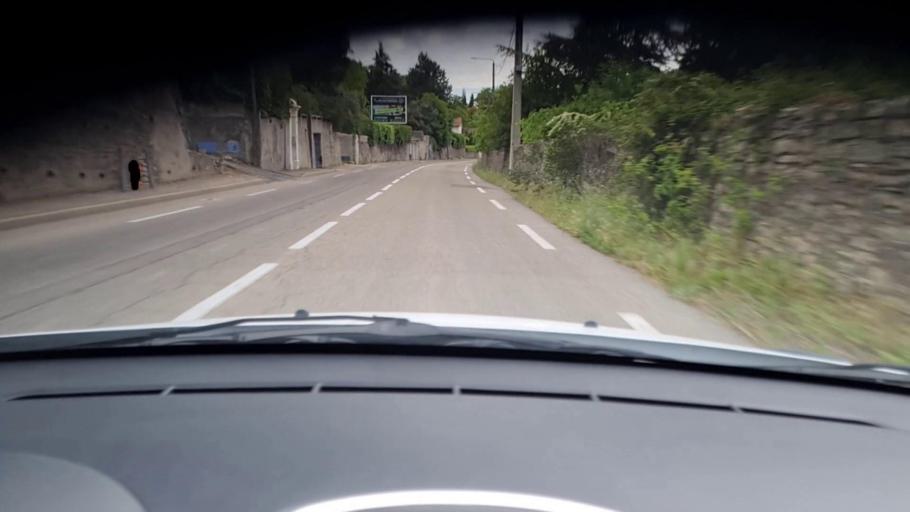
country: FR
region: Languedoc-Roussillon
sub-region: Departement du Gard
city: Nimes
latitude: 43.8607
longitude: 4.3774
